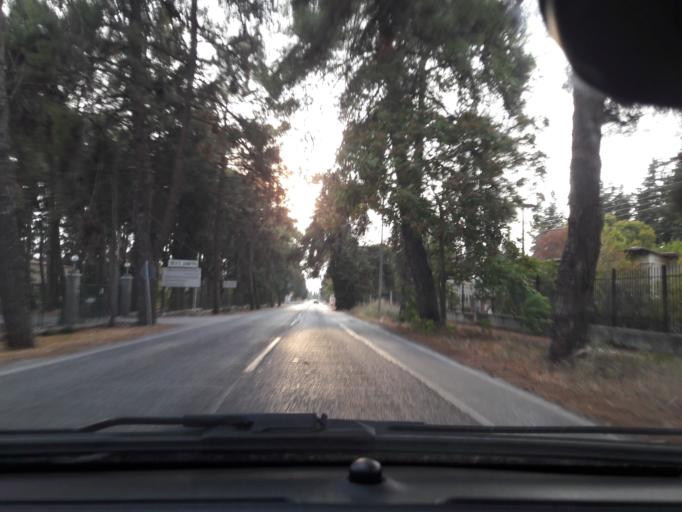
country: GR
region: Central Macedonia
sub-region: Nomos Thessalonikis
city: Thermi
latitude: 40.5389
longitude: 22.9994
